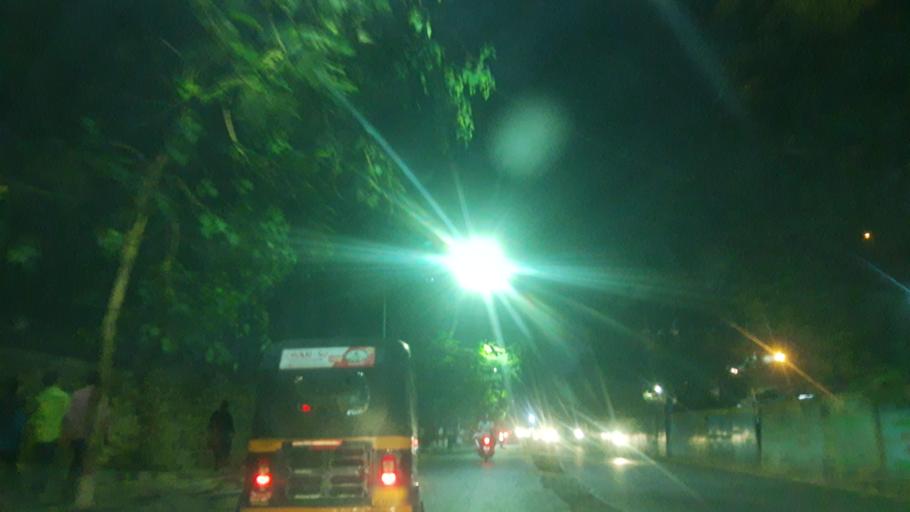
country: IN
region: Maharashtra
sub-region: Thane
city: Thane
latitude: 19.2050
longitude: 72.9688
